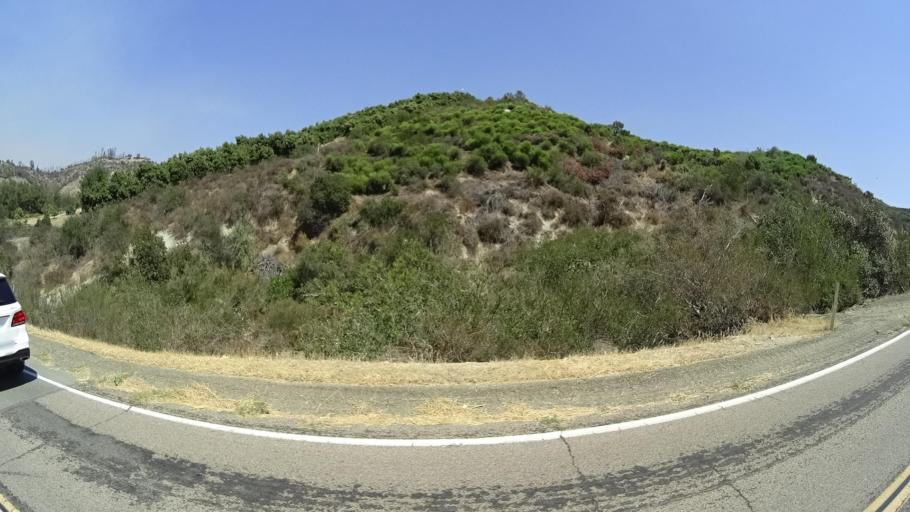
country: US
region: California
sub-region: San Diego County
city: Fallbrook
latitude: 33.4197
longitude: -117.3047
